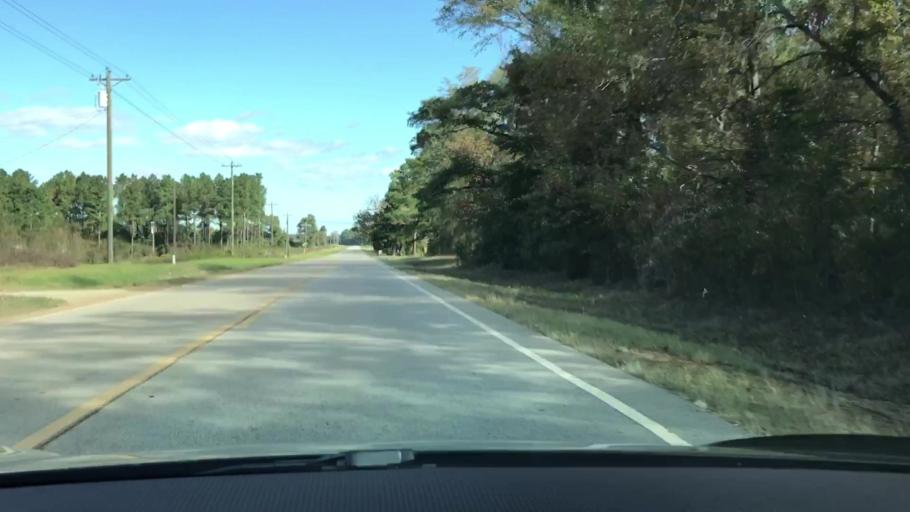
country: US
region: Georgia
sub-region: Jefferson County
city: Wrens
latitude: 33.1643
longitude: -82.4559
